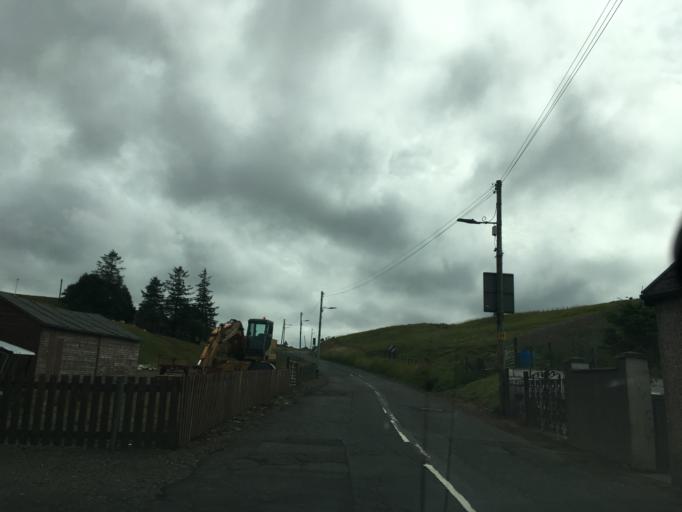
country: GB
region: Scotland
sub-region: South Lanarkshire
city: Douglas
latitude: 55.4124
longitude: -3.7635
